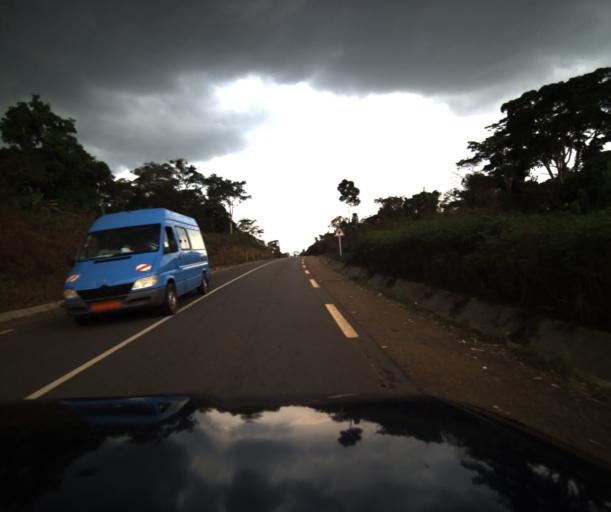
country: CM
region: Centre
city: Mbankomo
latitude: 3.6877
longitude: 11.3525
